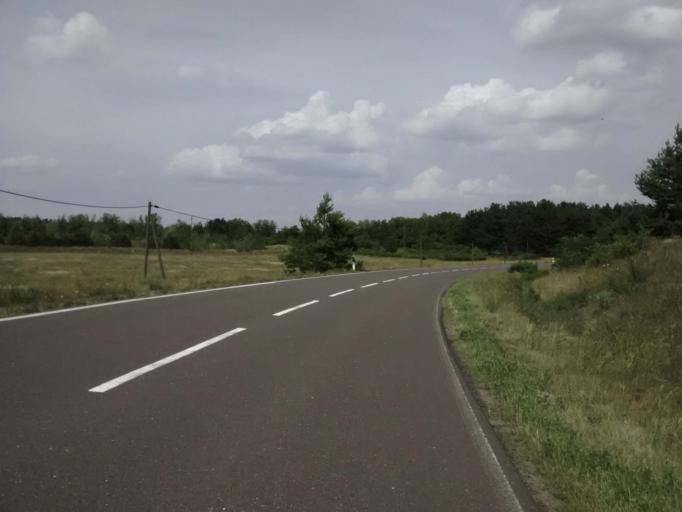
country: DE
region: Saxony-Anhalt
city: Hohenwarthe
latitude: 52.2384
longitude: 11.7279
